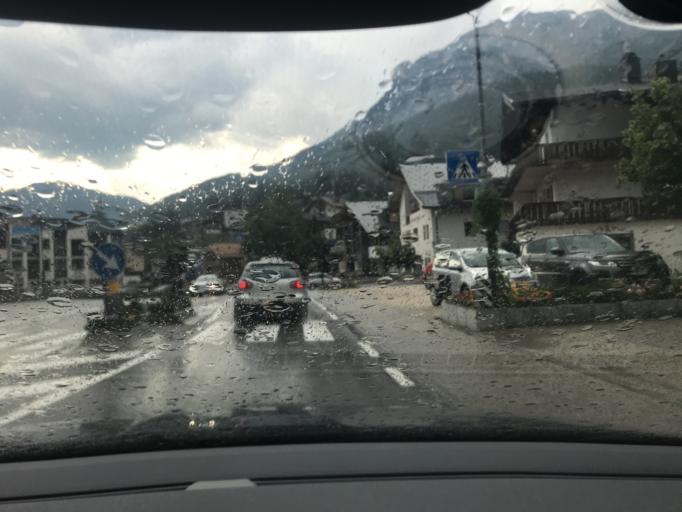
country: IT
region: Trentino-Alto Adige
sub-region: Bolzano
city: Badia
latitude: 46.6111
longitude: 11.8938
